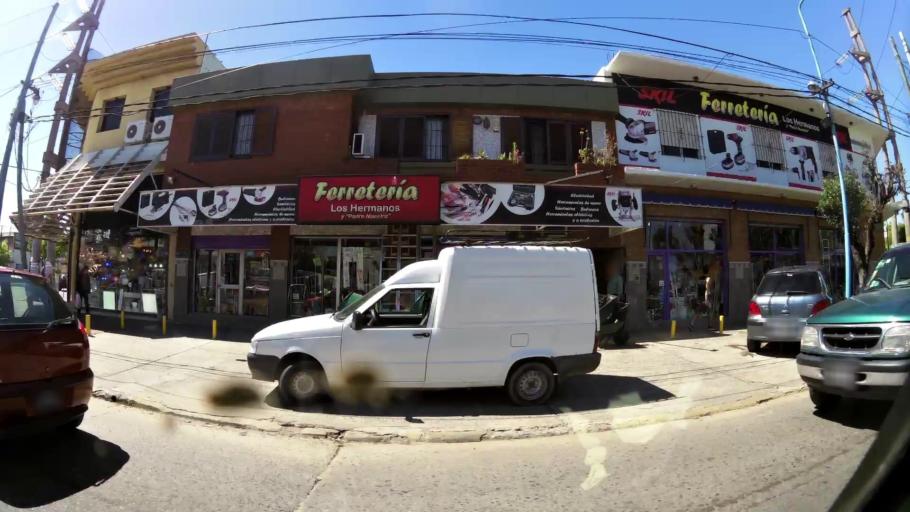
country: AR
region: Buenos Aires
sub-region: Partido de Quilmes
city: Quilmes
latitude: -34.7140
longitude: -58.3020
